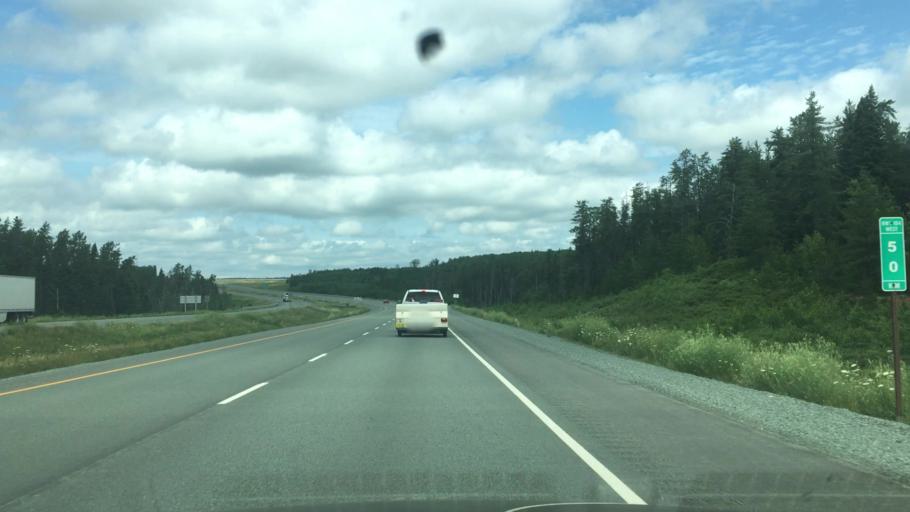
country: CA
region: Nova Scotia
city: Oxford
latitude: 45.6841
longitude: -63.7648
